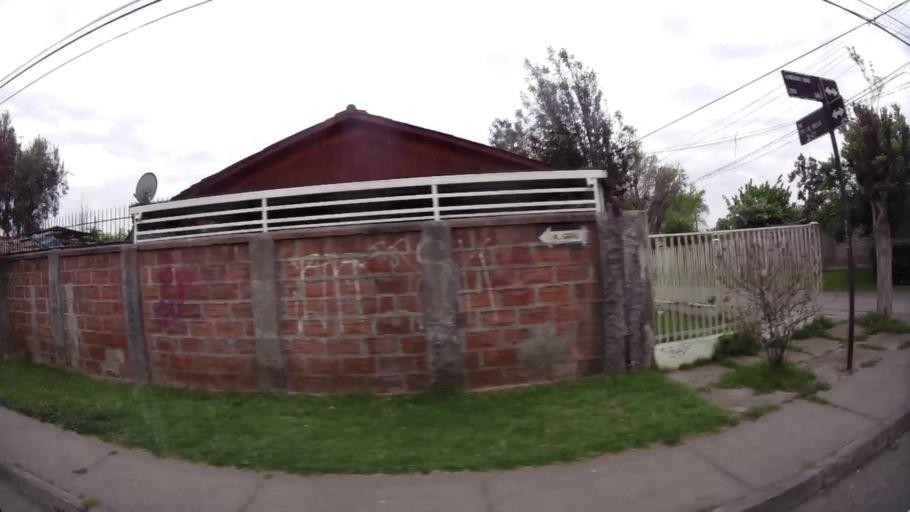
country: CL
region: Santiago Metropolitan
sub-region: Provincia de Santiago
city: Lo Prado
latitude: -33.5024
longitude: -70.7472
